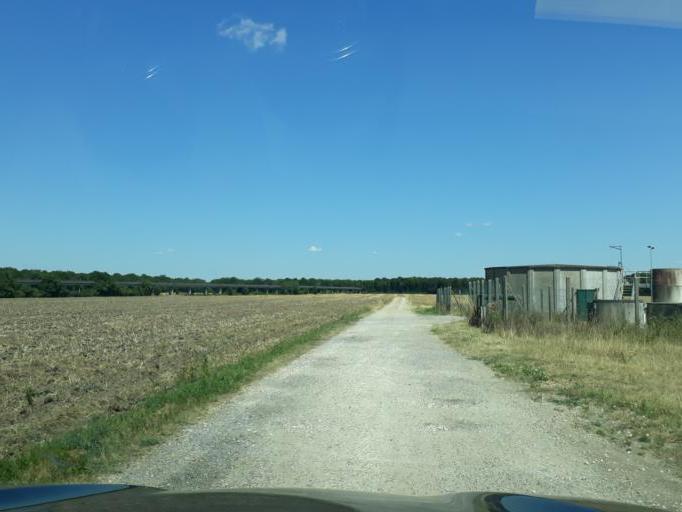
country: FR
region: Centre
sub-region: Departement du Loiret
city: Chevilly
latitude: 47.9962
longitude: 1.8864
